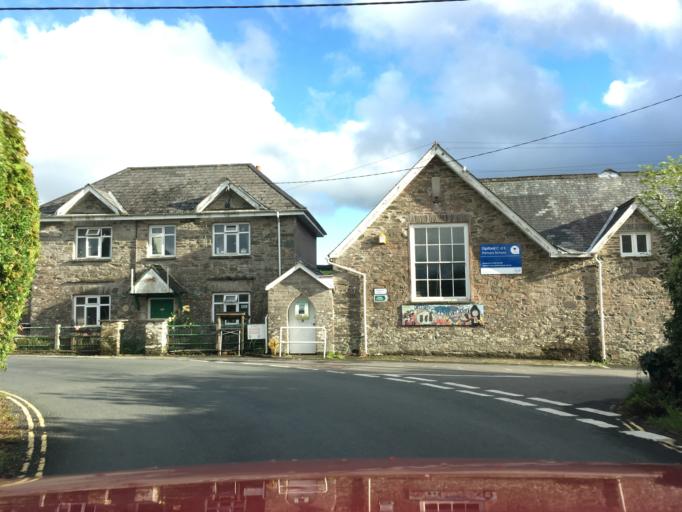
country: GB
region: England
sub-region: Devon
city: South Brent
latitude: 50.3969
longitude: -3.7912
